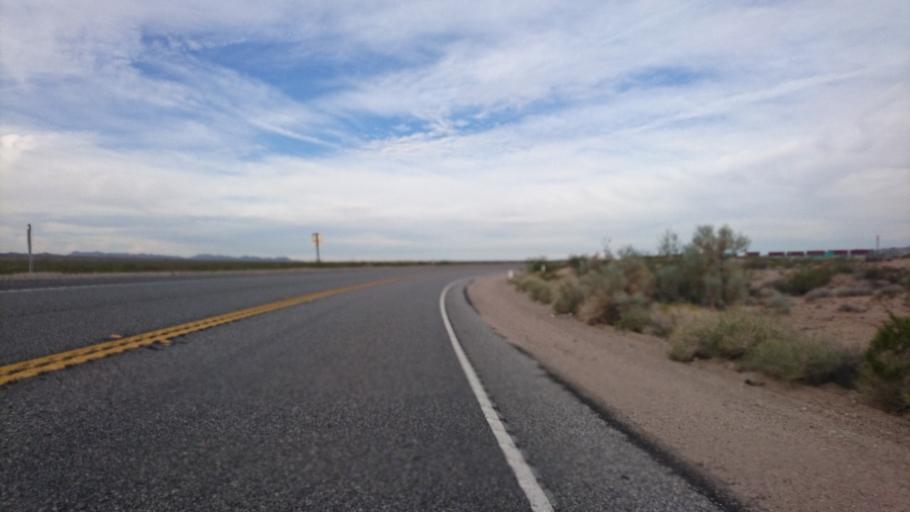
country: US
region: Arizona
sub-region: Mohave County
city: Willow Valley
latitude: 34.9401
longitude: -114.8215
